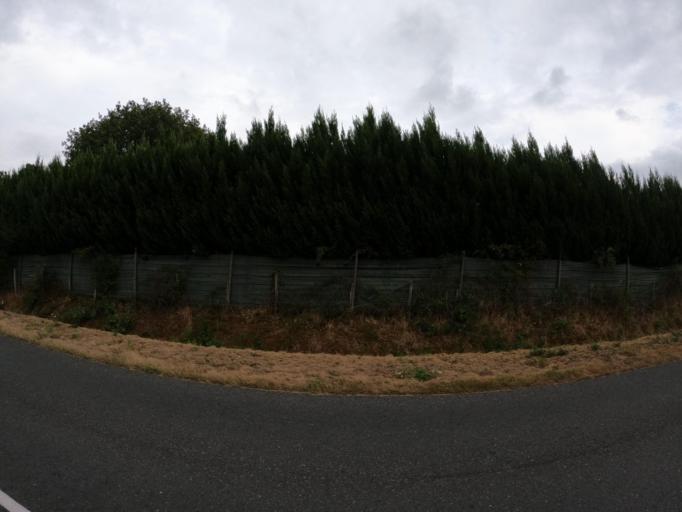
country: FR
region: Pays de la Loire
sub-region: Departement de Maine-et-Loire
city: Le Longeron
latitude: 47.0367
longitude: -1.0385
